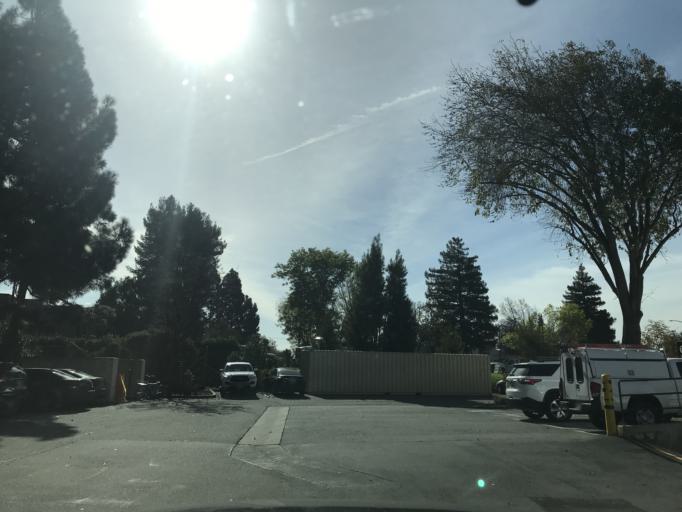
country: US
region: California
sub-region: San Mateo County
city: East Palo Alto
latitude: 37.4768
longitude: -122.1461
